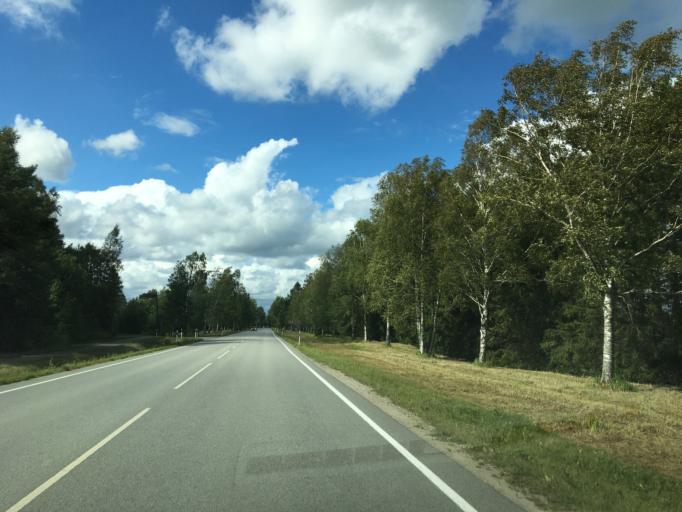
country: EE
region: Paernumaa
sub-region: Vaendra vald (alev)
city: Vandra
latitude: 58.6463
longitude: 25.0707
